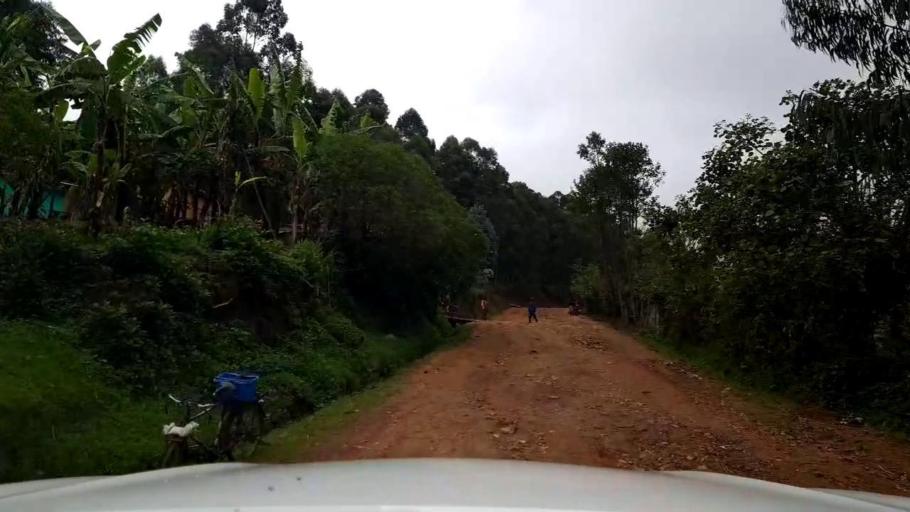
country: RW
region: Northern Province
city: Musanze
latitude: -1.6109
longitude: 29.7683
